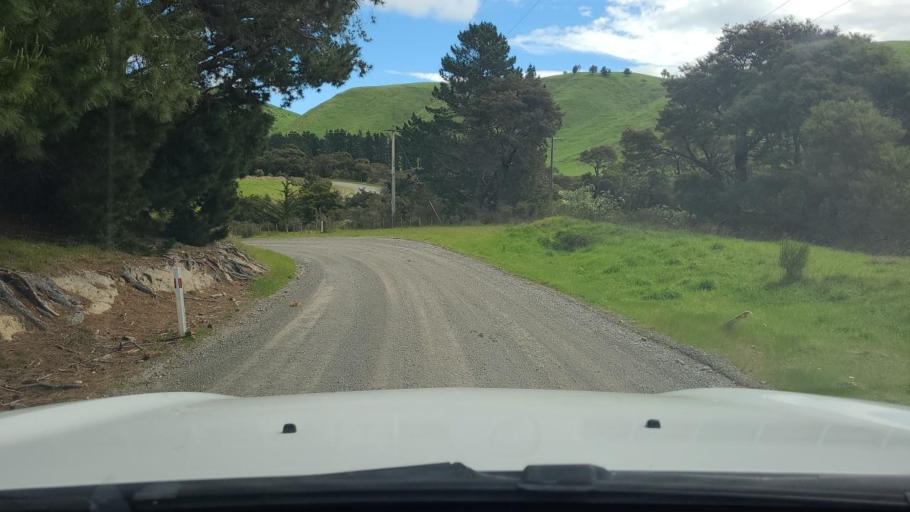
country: NZ
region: Wellington
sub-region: South Wairarapa District
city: Waipawa
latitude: -41.3208
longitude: 175.4134
